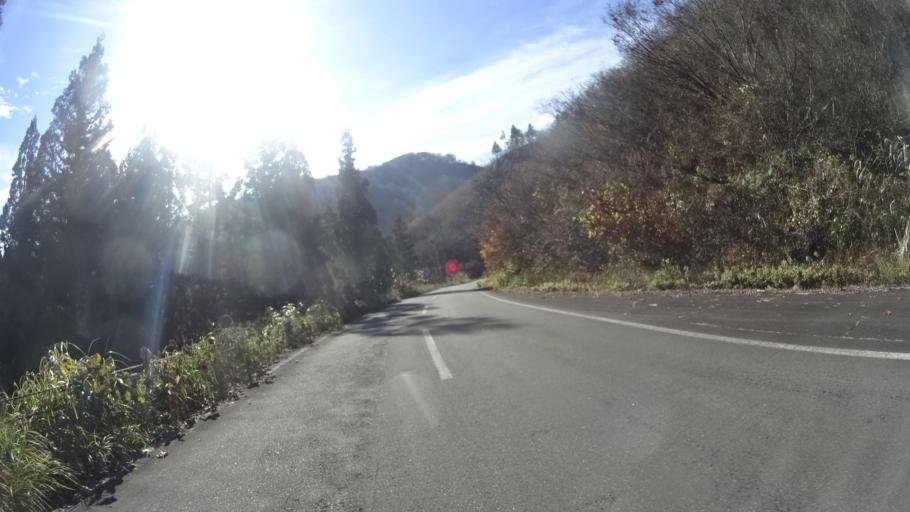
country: JP
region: Niigata
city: Muikamachi
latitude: 37.1848
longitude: 139.0811
